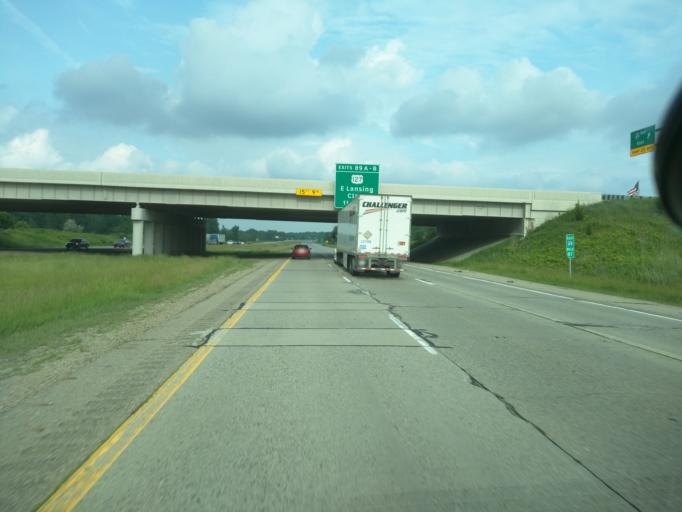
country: US
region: Michigan
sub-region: Clinton County
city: DeWitt
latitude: 42.8174
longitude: -84.5438
